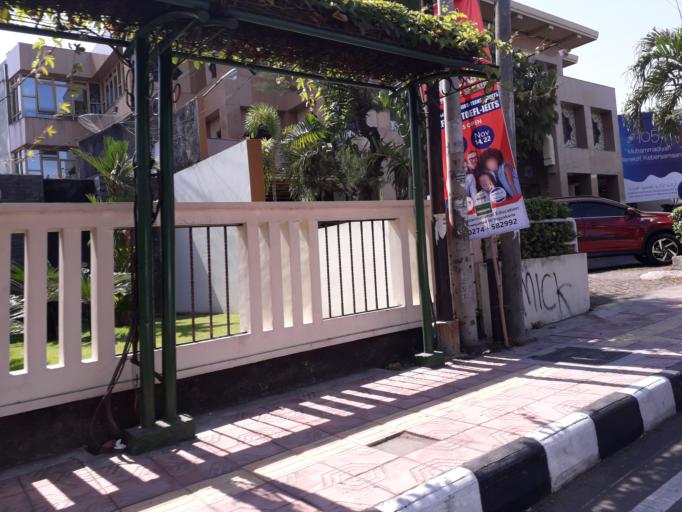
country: ID
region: Daerah Istimewa Yogyakarta
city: Yogyakarta
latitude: -7.7786
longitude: 110.3757
